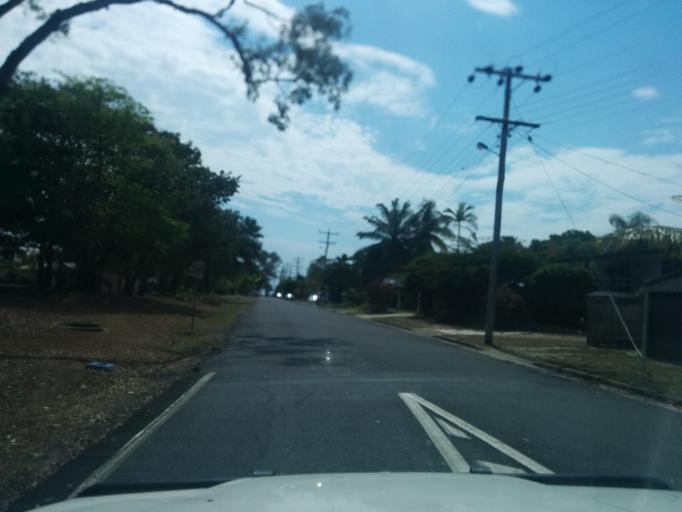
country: AU
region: Queensland
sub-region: Cairns
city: Yorkeys Knob
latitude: -16.8424
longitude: 145.7396
